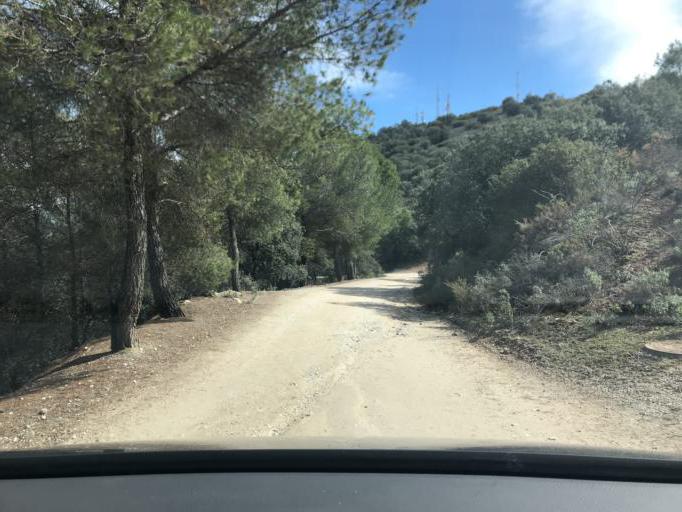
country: ES
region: Andalusia
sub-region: Provincia de Granada
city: Atarfe
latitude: 37.2475
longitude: -3.6850
